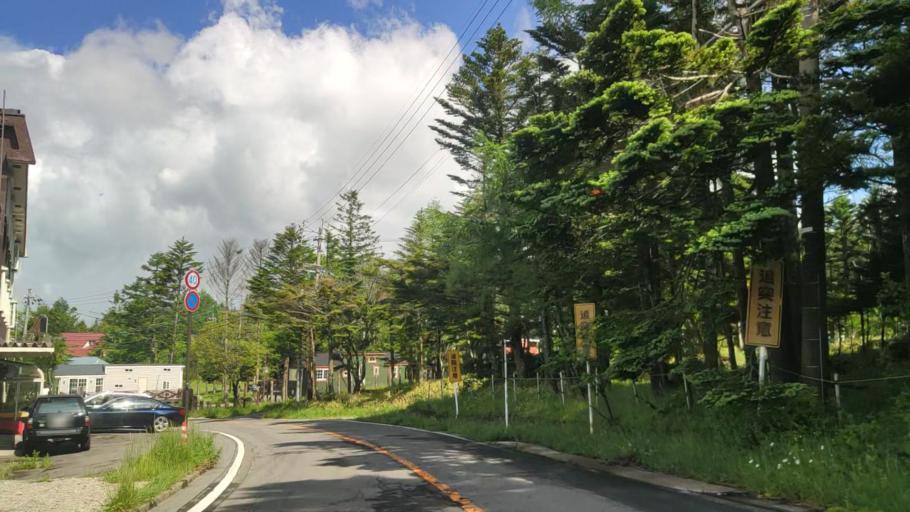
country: JP
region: Nagano
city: Suwa
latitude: 36.0985
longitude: 138.1627
